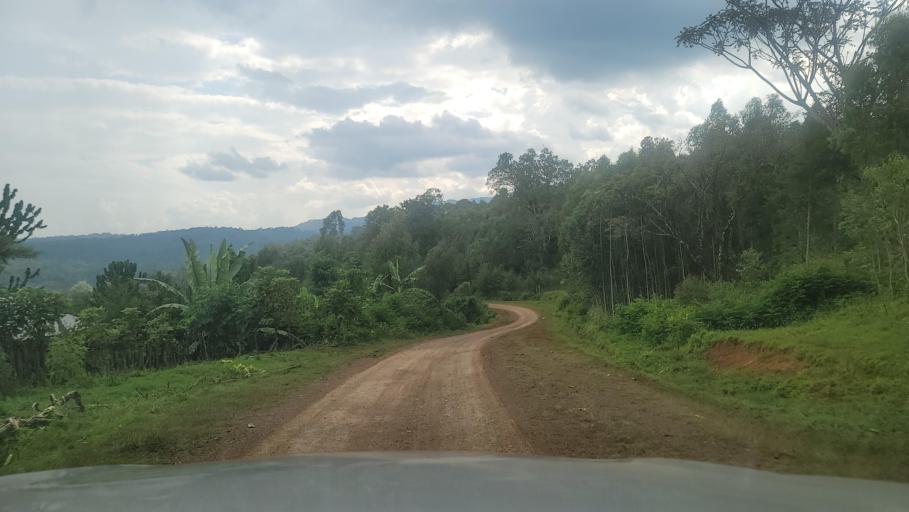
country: ET
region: Southern Nations, Nationalities, and People's Region
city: Bonga
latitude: 7.6994
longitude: 36.2488
